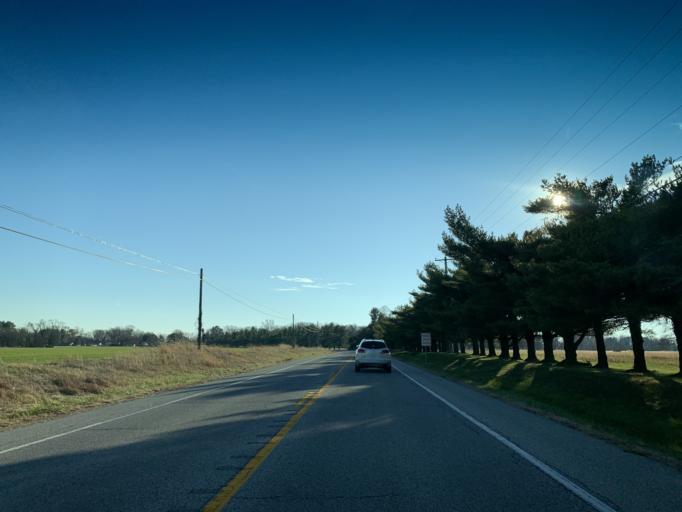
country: US
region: Delaware
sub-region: New Castle County
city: Middletown
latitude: 39.3749
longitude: -75.8824
